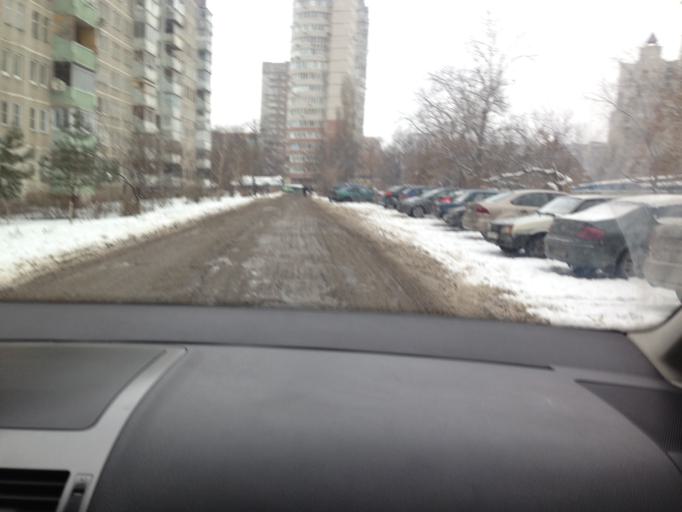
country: RU
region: Voronezj
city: Voronezh
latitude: 51.6686
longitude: 39.1855
